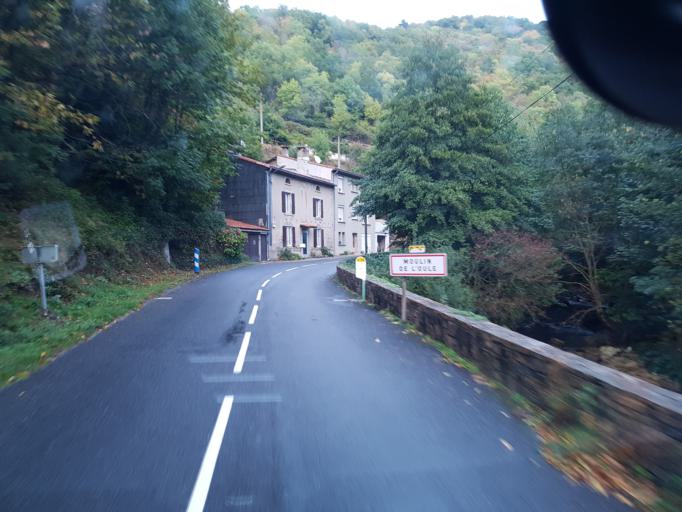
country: FR
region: Midi-Pyrenees
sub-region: Departement du Tarn
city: Mazamet
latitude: 43.4777
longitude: 2.3781
